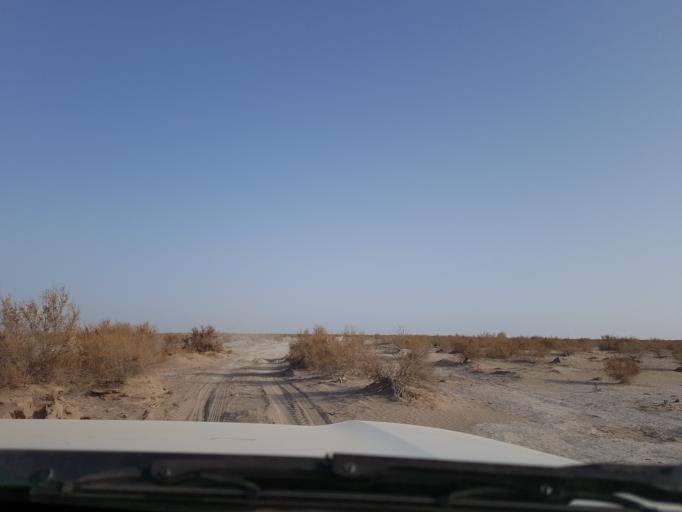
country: UZ
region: Karakalpakstan
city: Shumanay Shahri
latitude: 41.9998
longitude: 58.0922
